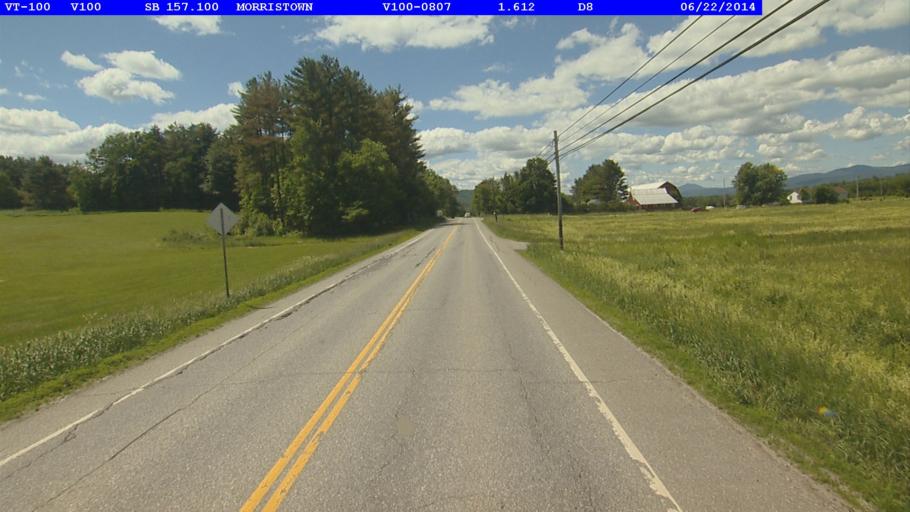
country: US
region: Vermont
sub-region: Lamoille County
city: Morristown
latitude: 44.5159
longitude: -72.6218
